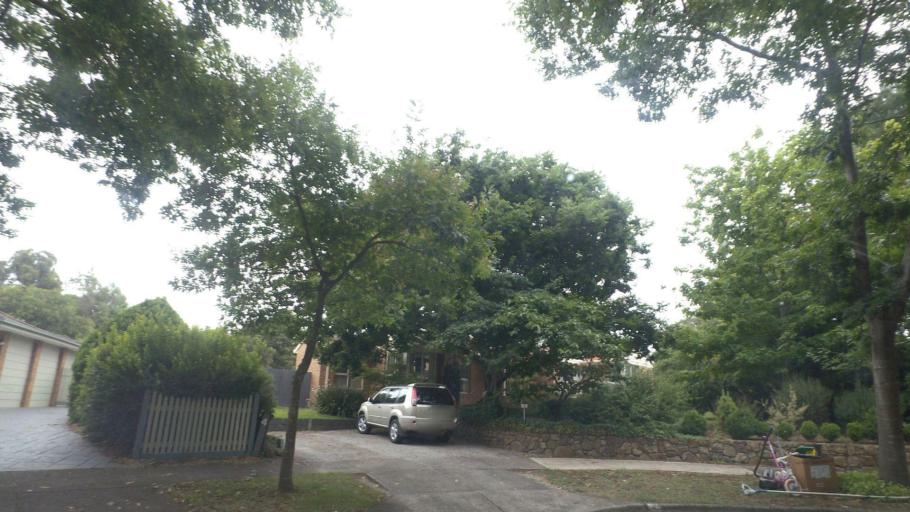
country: AU
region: Victoria
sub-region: Yarra Ranges
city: Kilsyth
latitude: -37.7776
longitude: 145.3354
